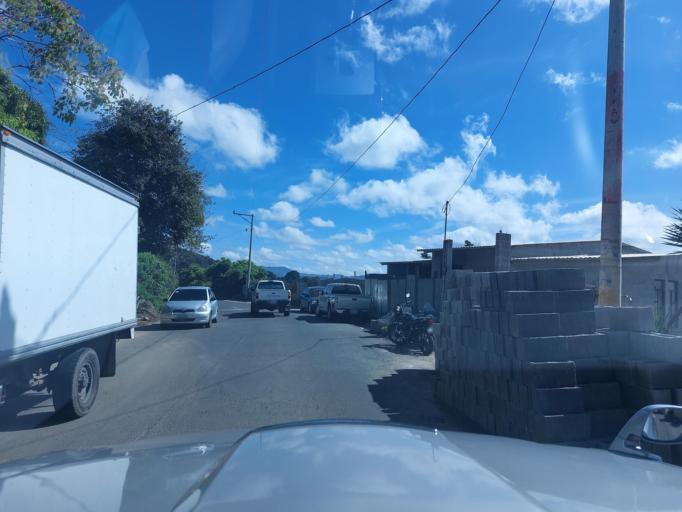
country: GT
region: Chimaltenango
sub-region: Municipio de Zaragoza
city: Zaragoza
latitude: 14.6487
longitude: -90.8971
